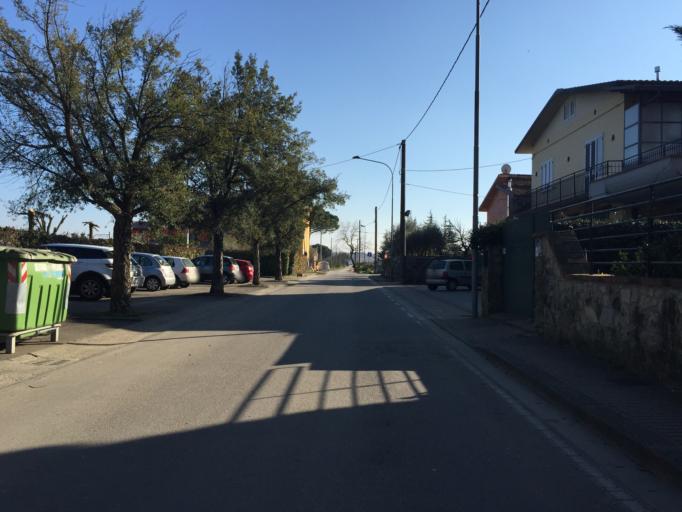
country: IT
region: Tuscany
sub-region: Provincia di Pistoia
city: Anchione
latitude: 43.8210
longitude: 10.7603
